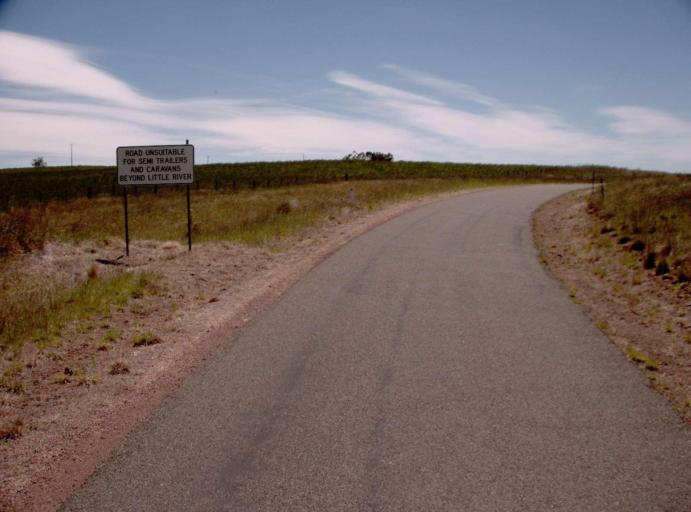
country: AU
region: New South Wales
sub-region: Snowy River
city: Jindabyne
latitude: -37.0997
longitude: 148.2530
